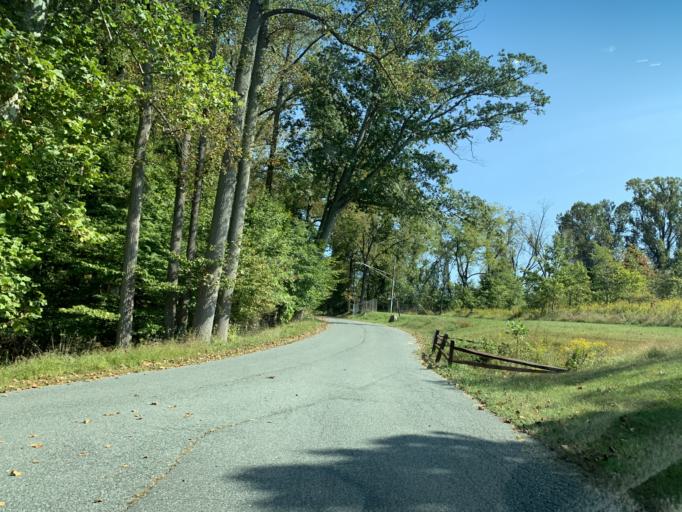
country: US
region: Maryland
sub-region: Harford County
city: Bel Air South
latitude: 39.4870
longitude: -76.3410
